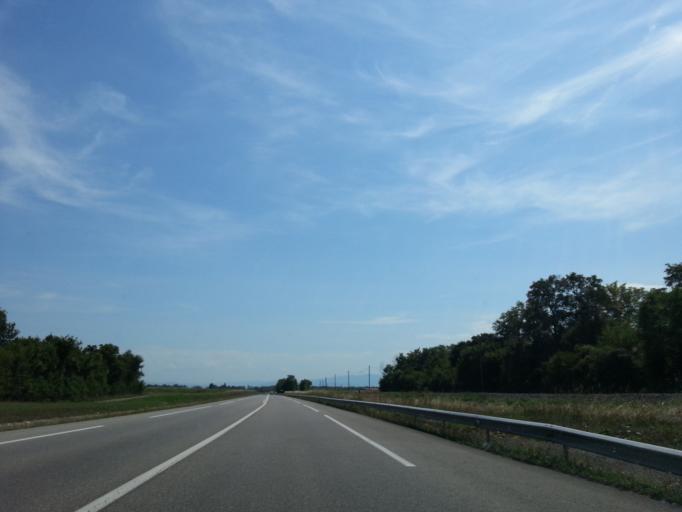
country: FR
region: Alsace
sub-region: Departement du Haut-Rhin
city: Wolfgantzen
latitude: 48.0352
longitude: 7.4882
